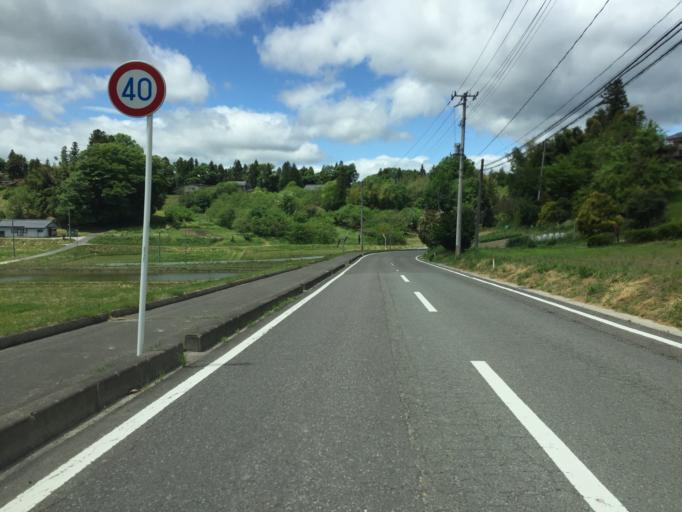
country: JP
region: Fukushima
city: Nihommatsu
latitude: 37.5550
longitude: 140.4647
